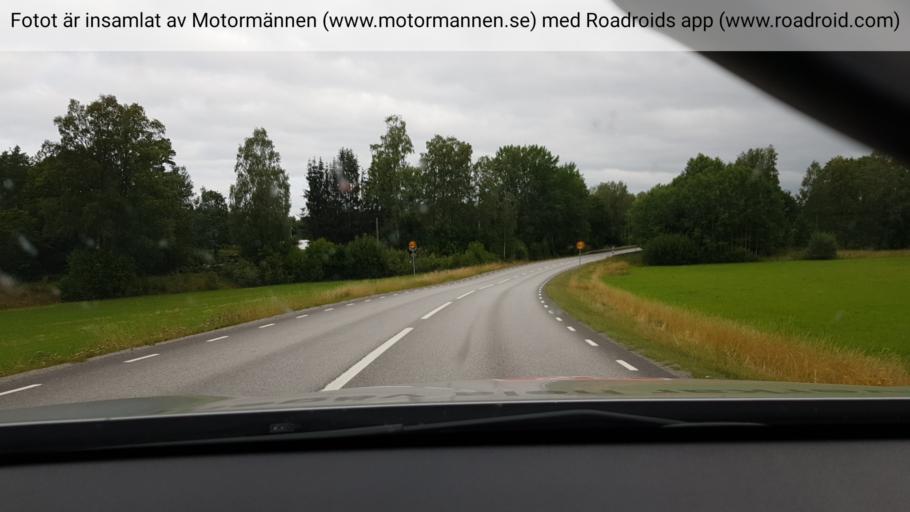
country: SE
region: Stockholm
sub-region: Norrtalje Kommun
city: Skanninge
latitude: 59.8922
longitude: 18.4904
